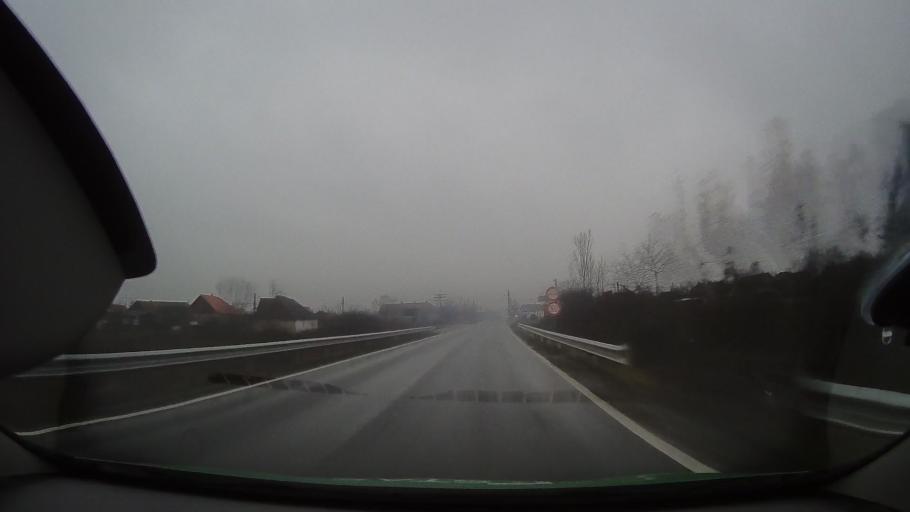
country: RO
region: Bihor
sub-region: Comuna Tinca
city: Tinca
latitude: 46.7388
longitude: 21.9410
